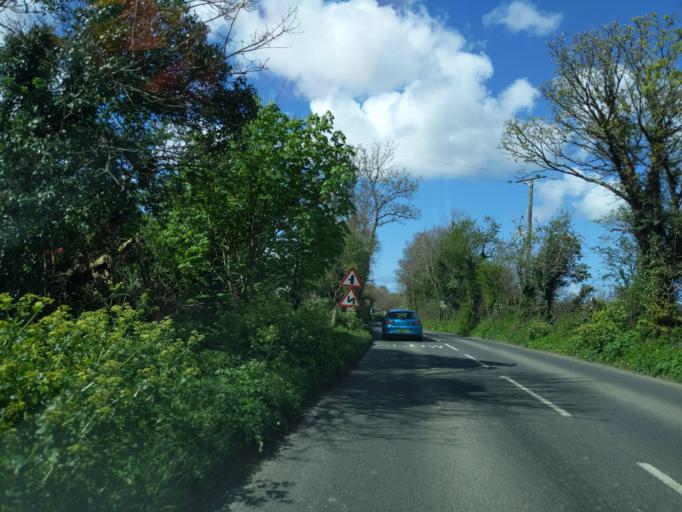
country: GB
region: England
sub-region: Cornwall
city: Wadebridge
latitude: 50.5260
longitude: -4.8317
